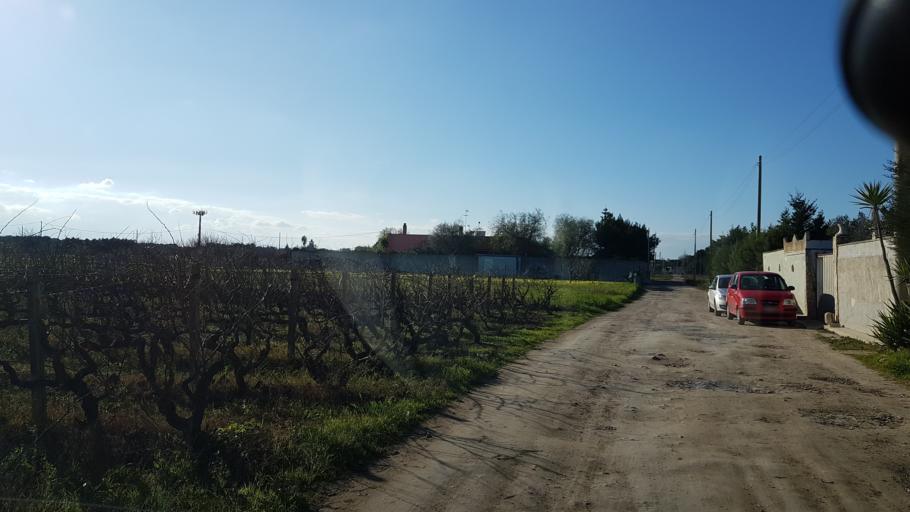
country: IT
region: Apulia
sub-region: Provincia di Brindisi
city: Tuturano
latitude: 40.5440
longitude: 17.9579
